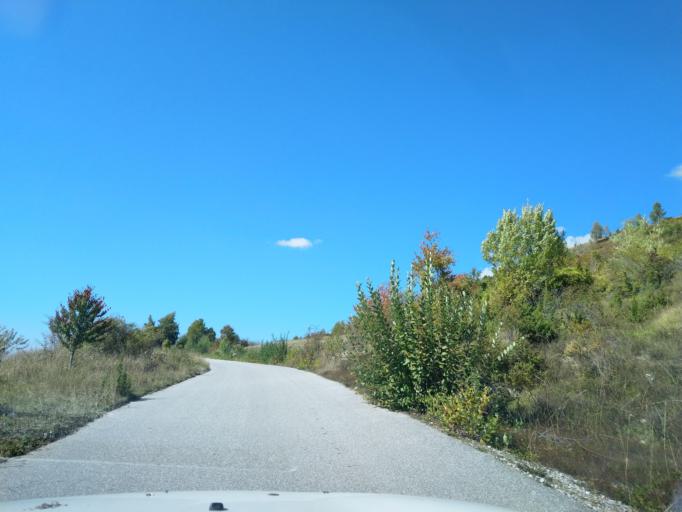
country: RS
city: Sokolovica
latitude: 43.2500
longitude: 20.3265
